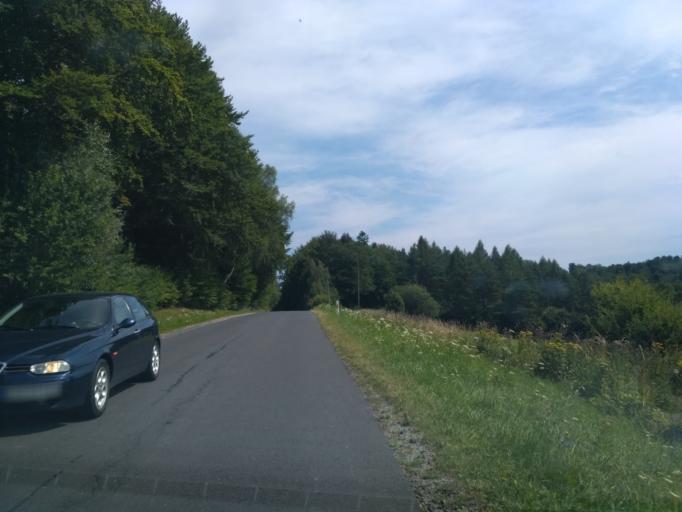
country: PL
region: Subcarpathian Voivodeship
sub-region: Powiat bieszczadzki
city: Czarna
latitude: 49.3073
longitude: 22.6235
